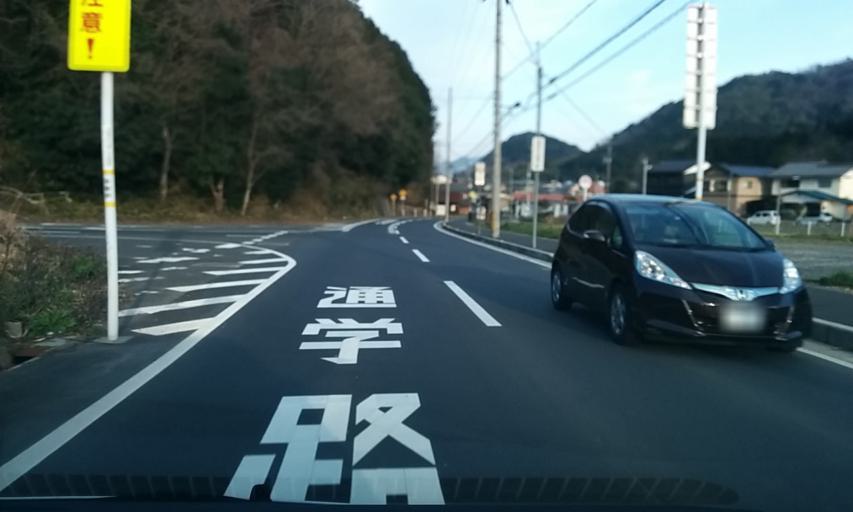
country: JP
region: Kyoto
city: Ayabe
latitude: 35.2891
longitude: 135.2535
